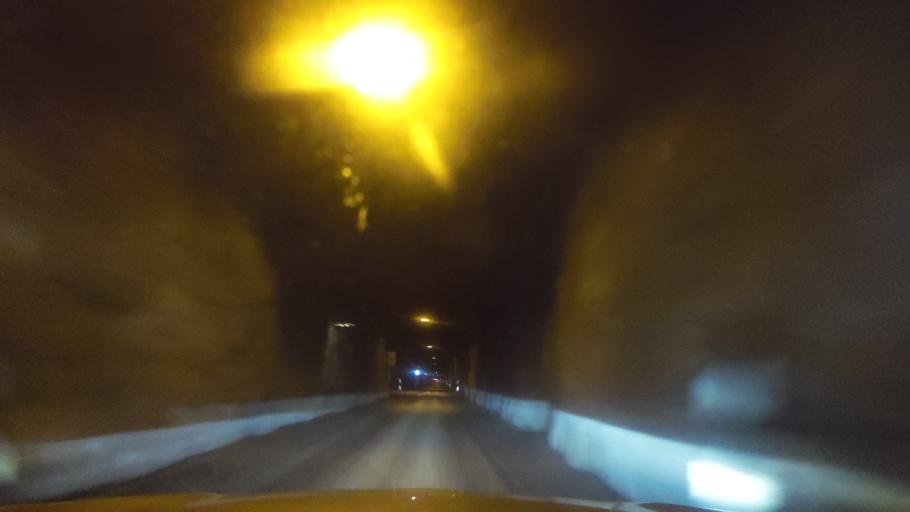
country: IS
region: Westfjords
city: Isafjoerdur
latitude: 66.0306
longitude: -23.3412
